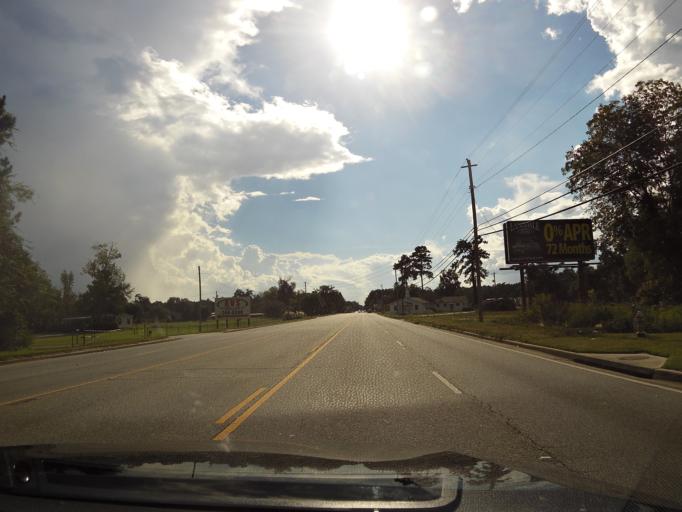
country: US
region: Georgia
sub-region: Lowndes County
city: Remerton
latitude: 30.8151
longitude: -83.3231
